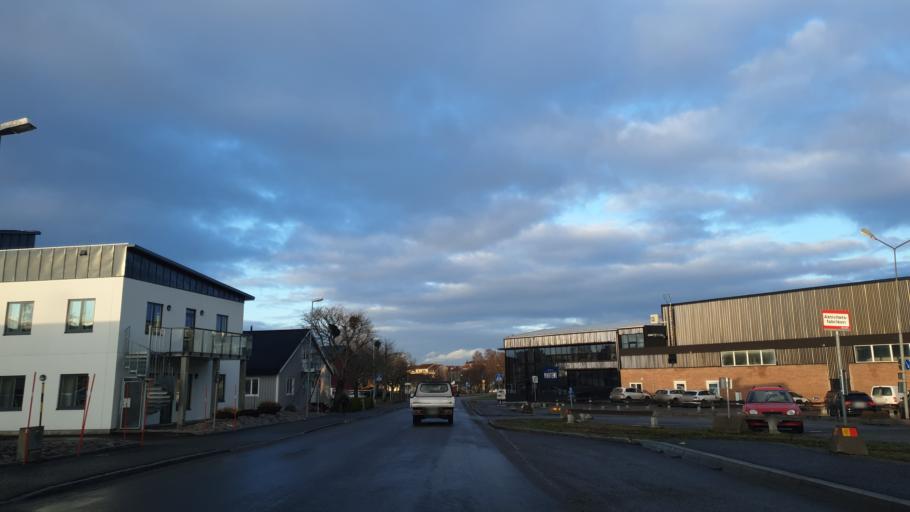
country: SE
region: Gaevleborg
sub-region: Hudiksvalls Kommun
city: Hudiksvall
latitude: 61.7244
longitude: 17.1269
